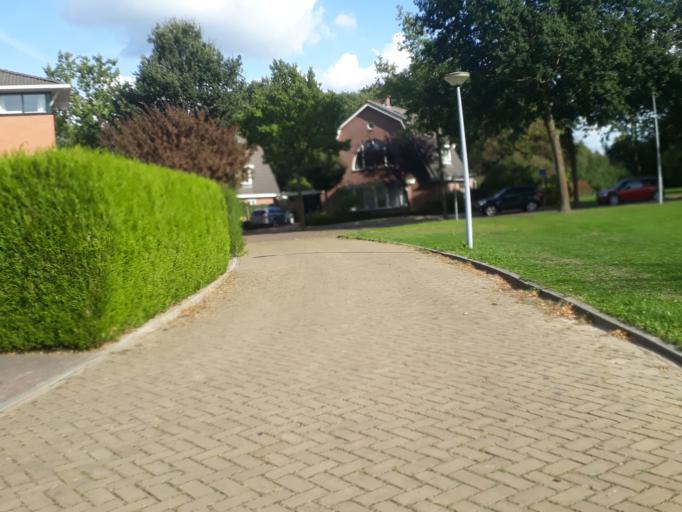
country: NL
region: Gelderland
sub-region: Gemeente Zevenaar
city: Zevenaar
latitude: 51.9402
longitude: 6.0567
